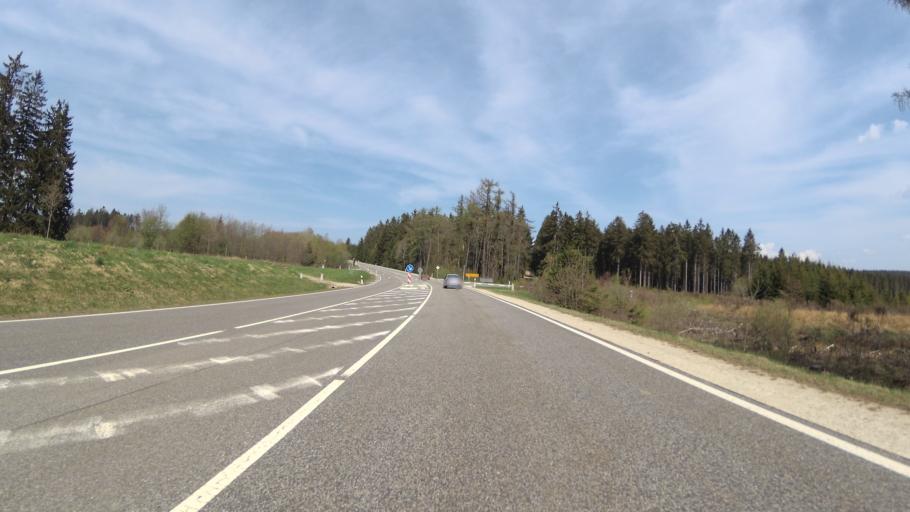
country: DE
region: Rheinland-Pfalz
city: Wirschweiler
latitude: 49.7655
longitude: 7.1310
